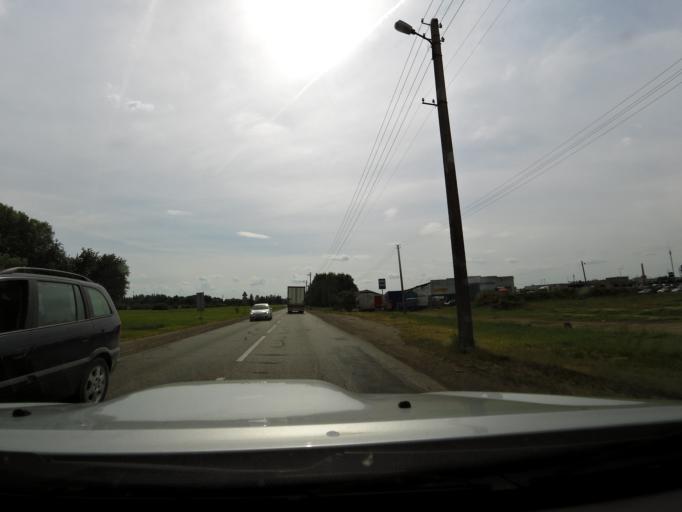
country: LT
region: Marijampoles apskritis
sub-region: Marijampole Municipality
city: Marijampole
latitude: 54.5650
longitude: 23.3837
